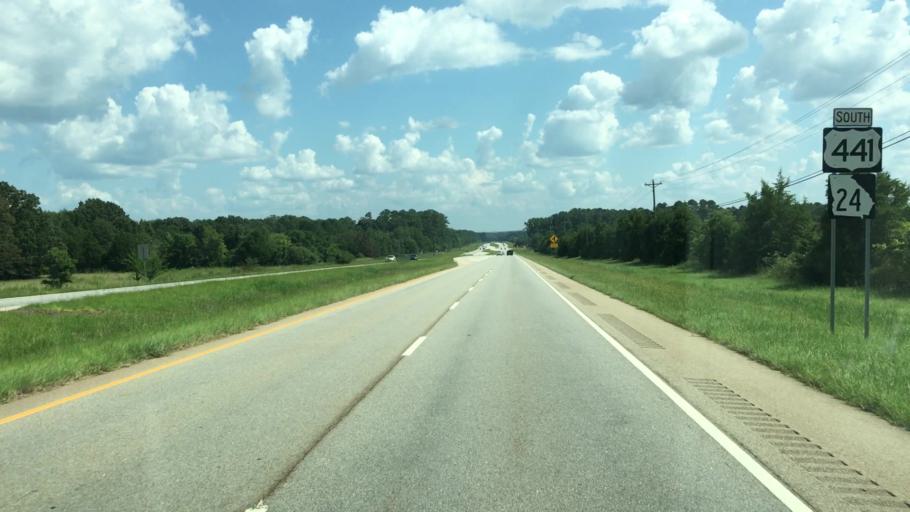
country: US
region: Georgia
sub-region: Putnam County
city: Eatonton
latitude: 33.2661
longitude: -83.3353
